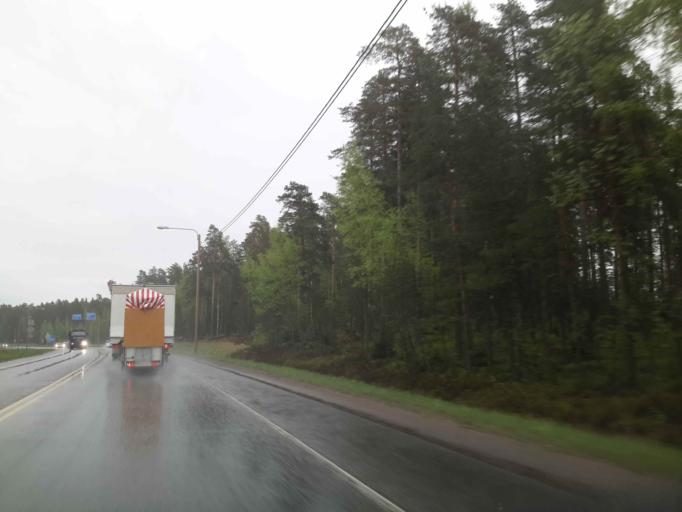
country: FI
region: Uusimaa
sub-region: Helsinki
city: Vihti
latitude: 60.3490
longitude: 24.3244
